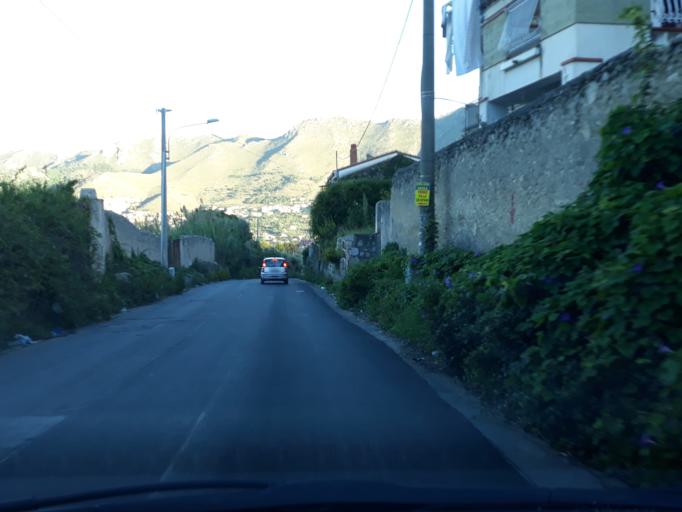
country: IT
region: Sicily
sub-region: Palermo
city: Monreale
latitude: 38.0735
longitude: 13.2915
